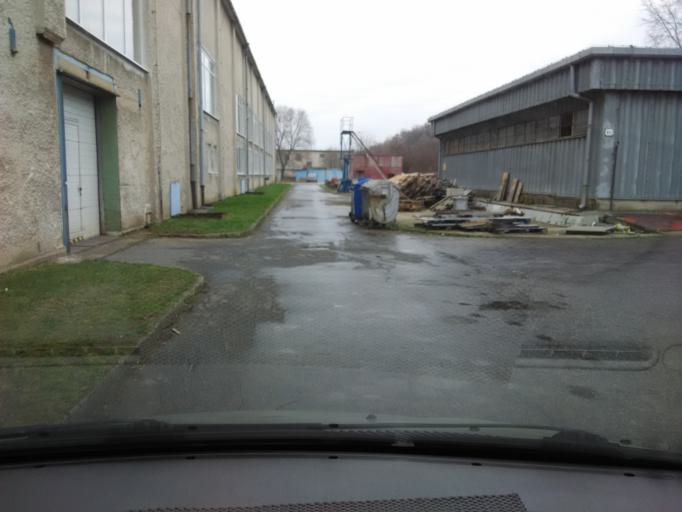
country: SK
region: Nitriansky
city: Tlmace
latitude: 48.2949
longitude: 18.5428
